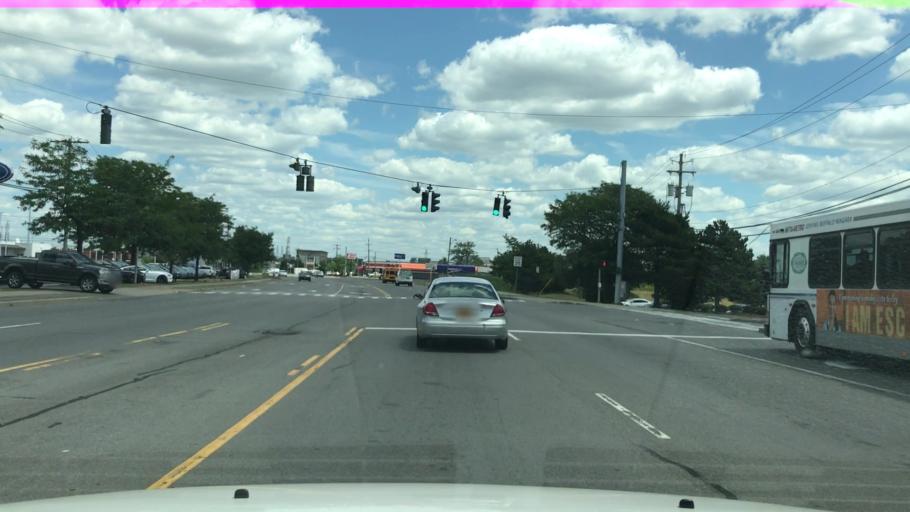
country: US
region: New York
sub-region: Erie County
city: Sloan
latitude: 42.9068
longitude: -78.7811
